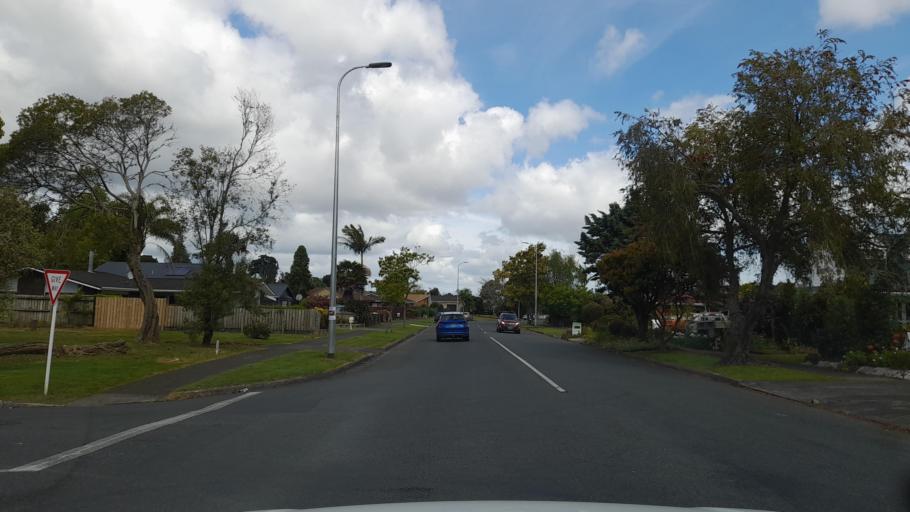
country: NZ
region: Northland
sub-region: Whangarei
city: Whangarei
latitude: -35.6875
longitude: 174.3002
